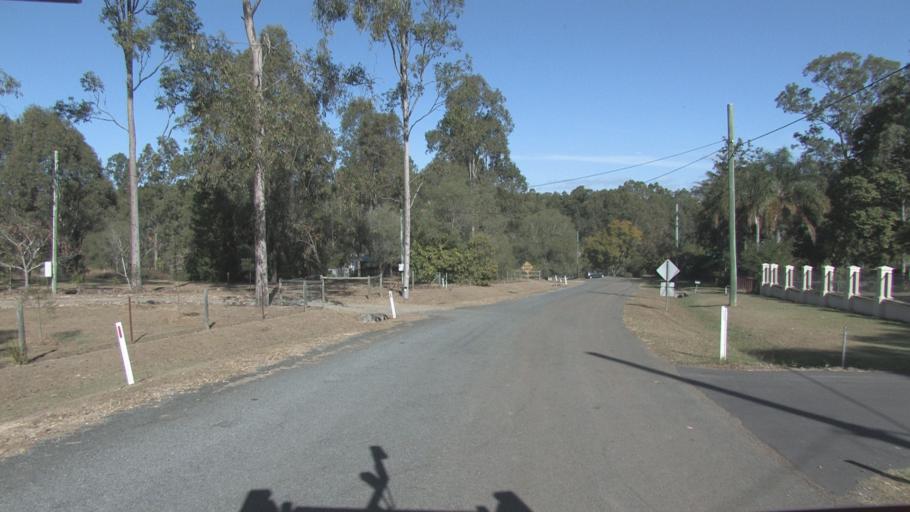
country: AU
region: Queensland
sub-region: Logan
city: Cedar Vale
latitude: -27.8570
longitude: 152.9873
